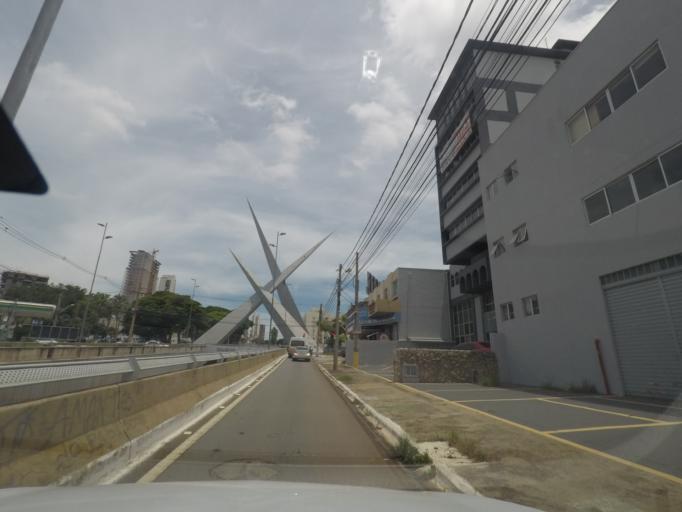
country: BR
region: Goias
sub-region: Goiania
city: Goiania
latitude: -16.6903
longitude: -49.2618
